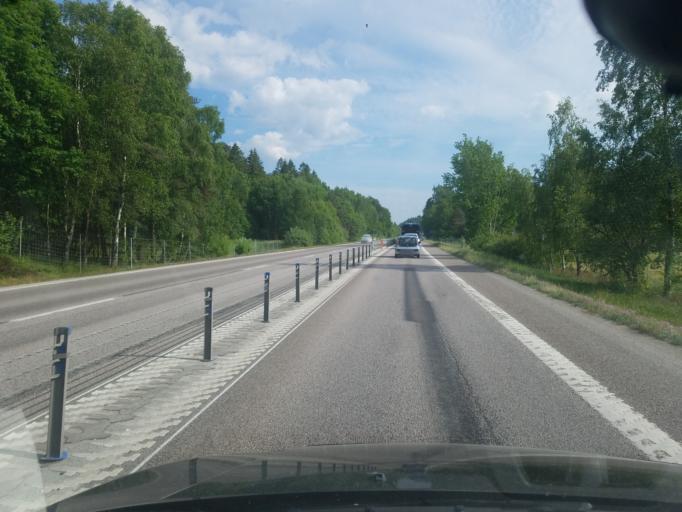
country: SE
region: Vaestra Goetaland
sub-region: Goteborg
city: Billdal
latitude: 57.6056
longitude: 11.9506
